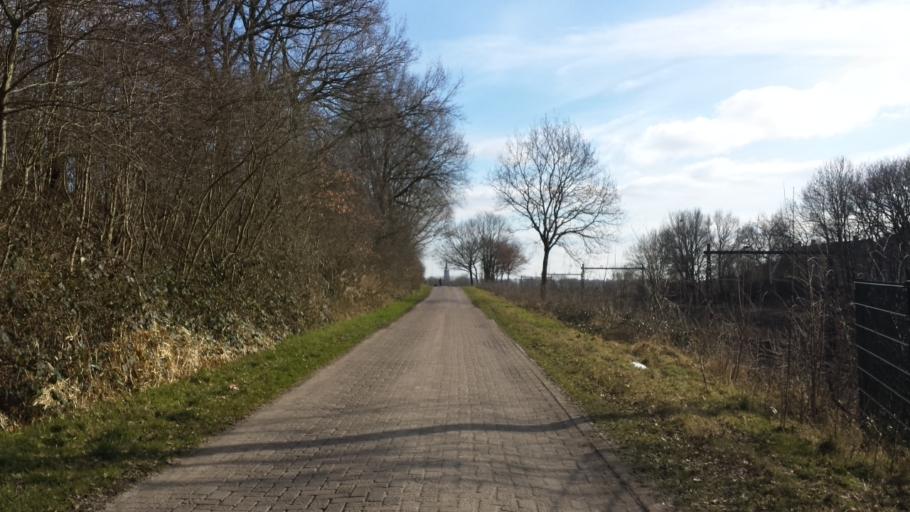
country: NL
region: Overijssel
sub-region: Gemeente Steenwijkerland
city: Tuk
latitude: 52.8043
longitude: 6.0921
